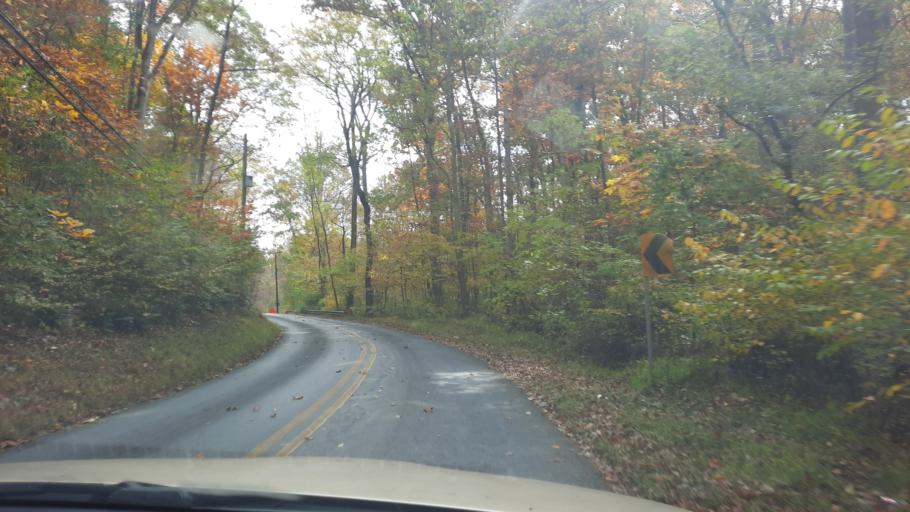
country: US
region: Maryland
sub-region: Montgomery County
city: Germantown
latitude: 39.1581
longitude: -77.2397
